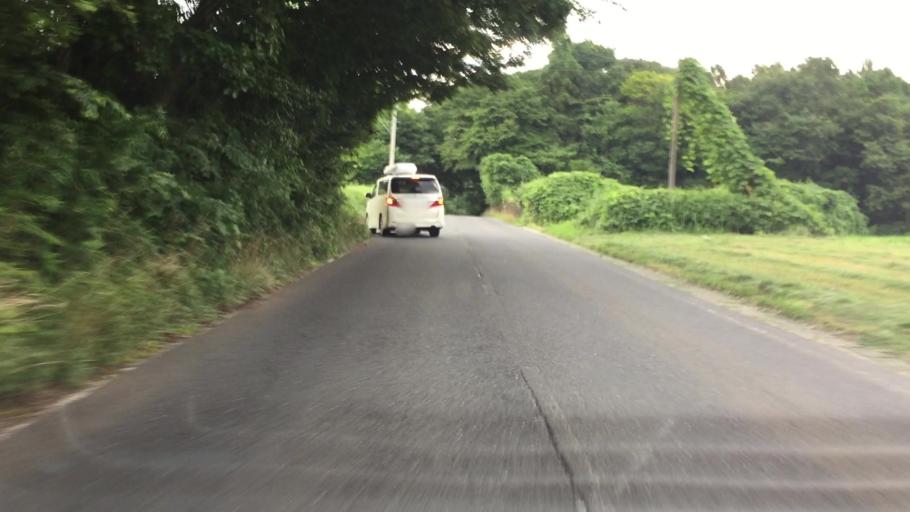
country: JP
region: Tochigi
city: Kuroiso
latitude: 37.0836
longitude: 140.0554
